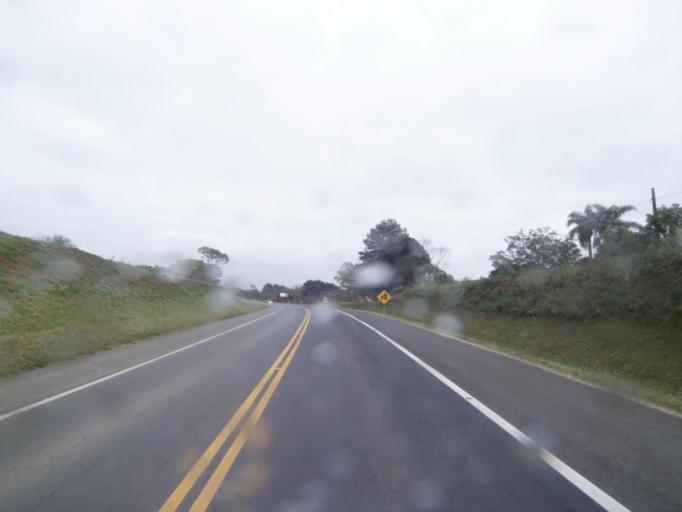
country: BR
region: Parana
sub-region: Palmeira
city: Palmeira
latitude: -25.4279
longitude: -50.1344
